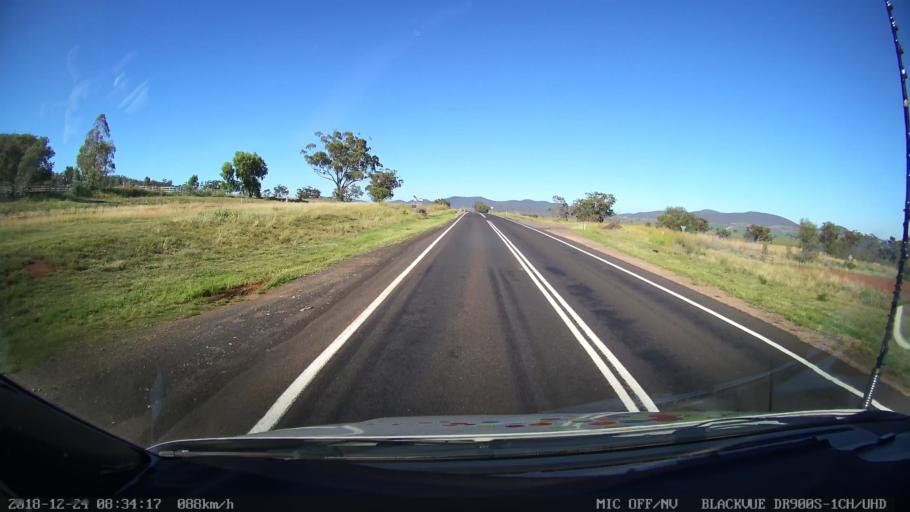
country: AU
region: New South Wales
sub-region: Liverpool Plains
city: Quirindi
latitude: -31.2916
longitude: 150.6727
